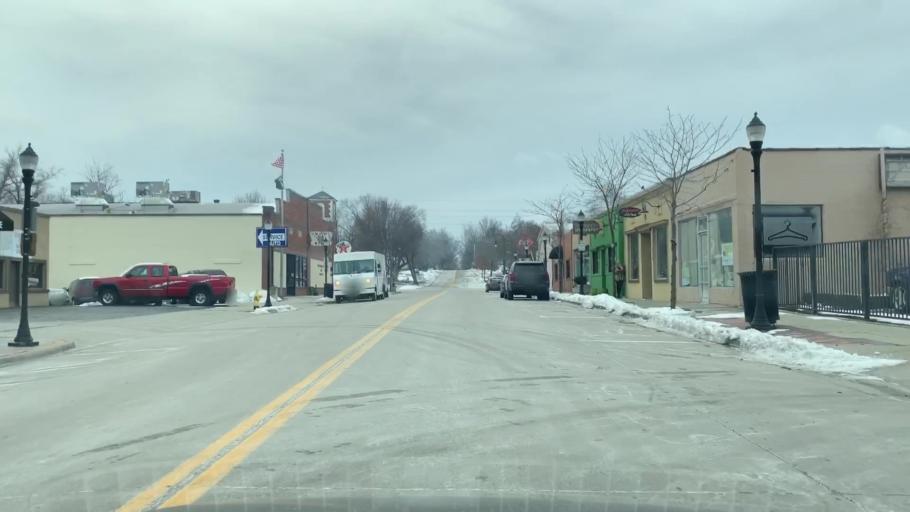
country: US
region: Missouri
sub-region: Jackson County
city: Lees Summit
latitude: 38.9120
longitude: -94.3759
